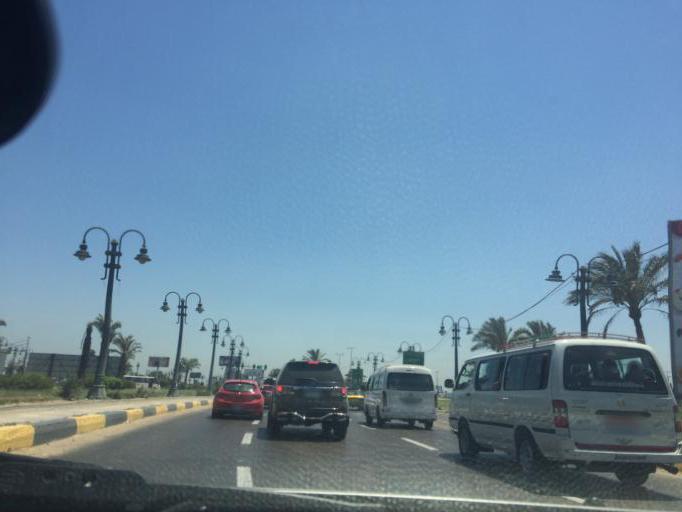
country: EG
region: Alexandria
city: Alexandria
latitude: 31.1706
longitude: 29.9339
